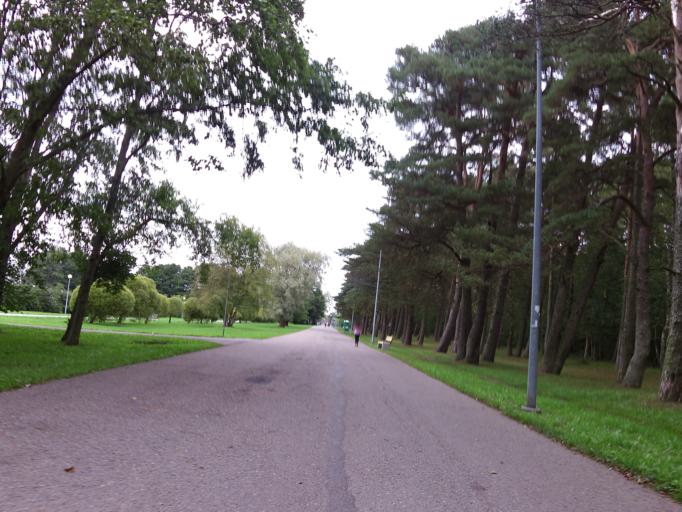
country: EE
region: Harju
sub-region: Tallinna linn
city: Tallinn
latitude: 59.4370
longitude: 24.6839
